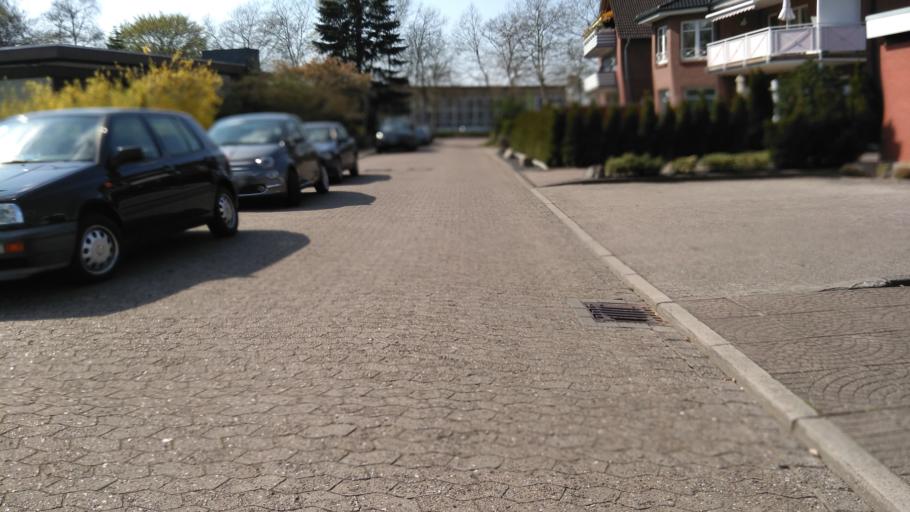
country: DE
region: Lower Saxony
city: Buxtehude
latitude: 53.4767
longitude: 9.6960
